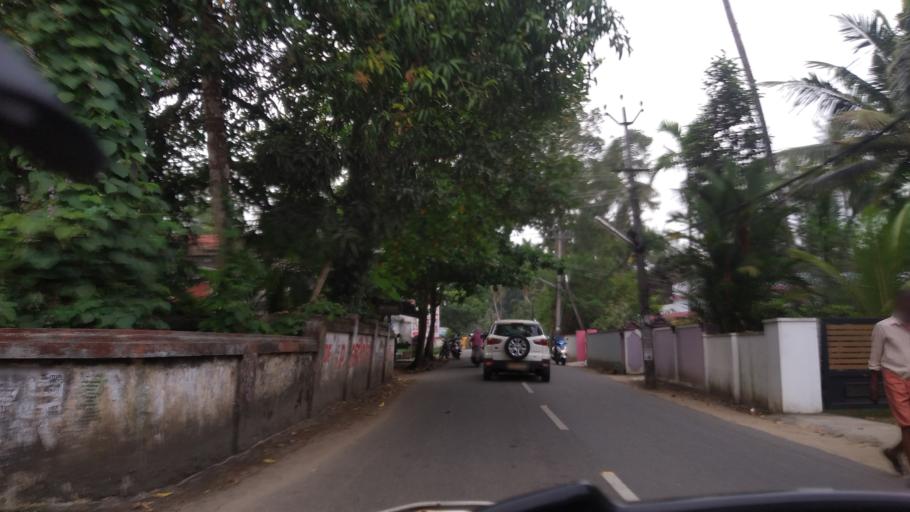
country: IN
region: Kerala
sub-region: Thrissur District
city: Kodungallur
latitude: 10.1418
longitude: 76.2175
